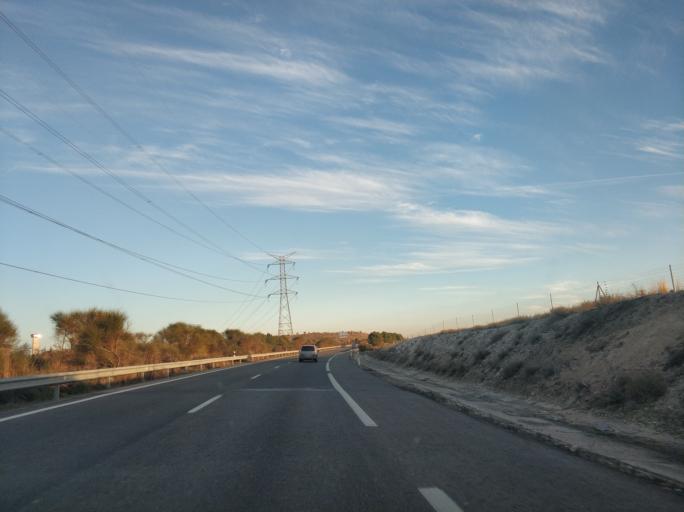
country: ES
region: Madrid
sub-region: Provincia de Madrid
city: Valdemoro
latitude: 40.2199
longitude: -3.6679
